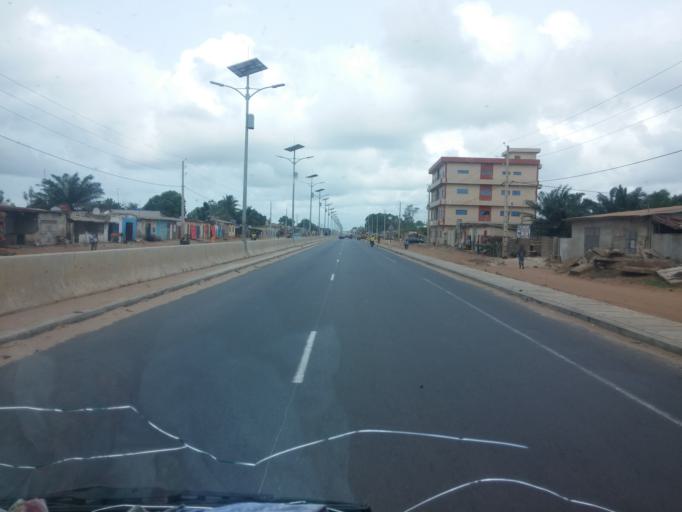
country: BJ
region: Atlantique
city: Hevie
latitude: 6.3872
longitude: 2.2316
